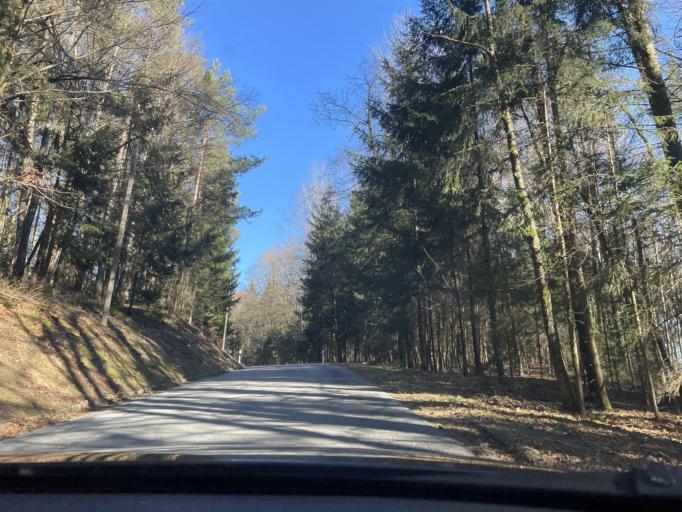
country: DE
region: Bavaria
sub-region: Lower Bavaria
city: Geiersthal
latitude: 49.0807
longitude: 12.9591
